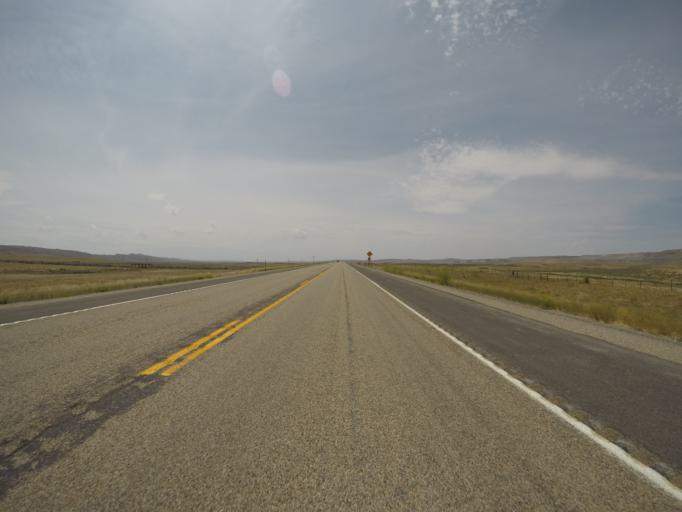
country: US
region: Wyoming
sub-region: Lincoln County
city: Kemmerer
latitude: 41.7344
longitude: -110.5649
